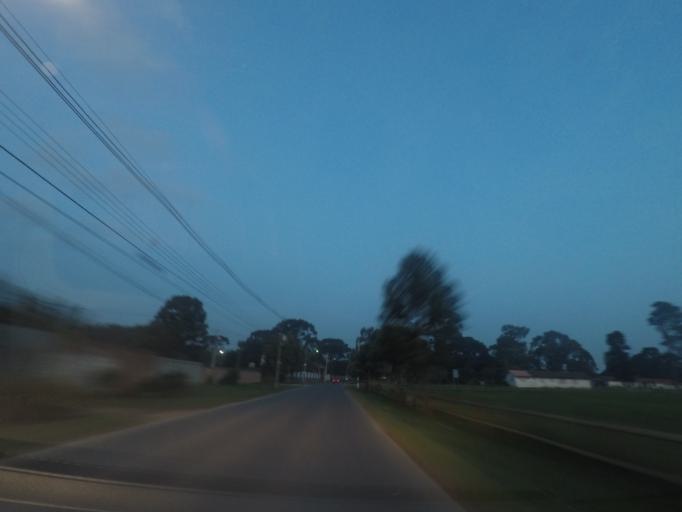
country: BR
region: Parana
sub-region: Pinhais
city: Pinhais
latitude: -25.4628
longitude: -49.1525
